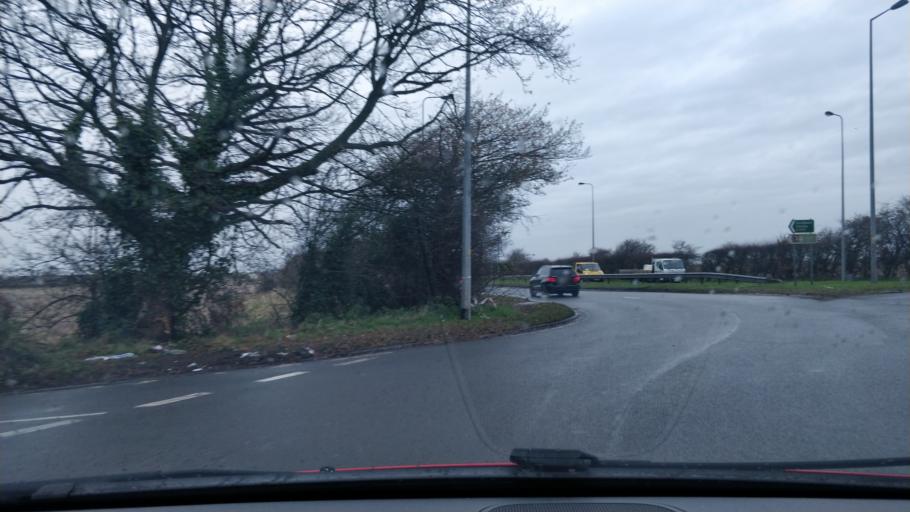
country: GB
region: England
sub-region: Sefton
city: Hightown
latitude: 53.5445
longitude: -3.0486
